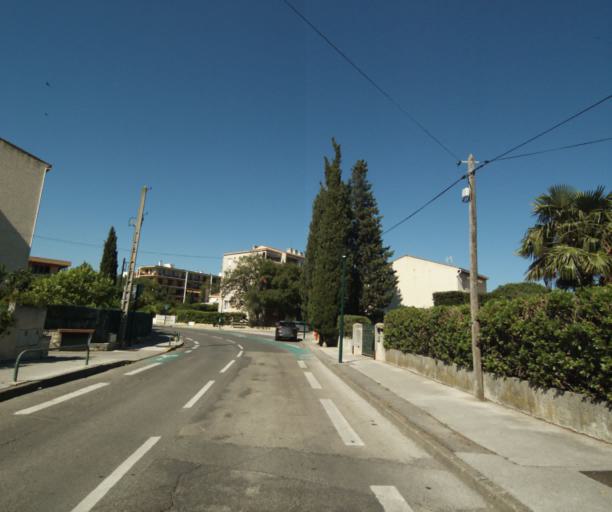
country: FR
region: Provence-Alpes-Cote d'Azur
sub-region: Departement du Var
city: La Garde
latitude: 43.1199
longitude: 6.0060
